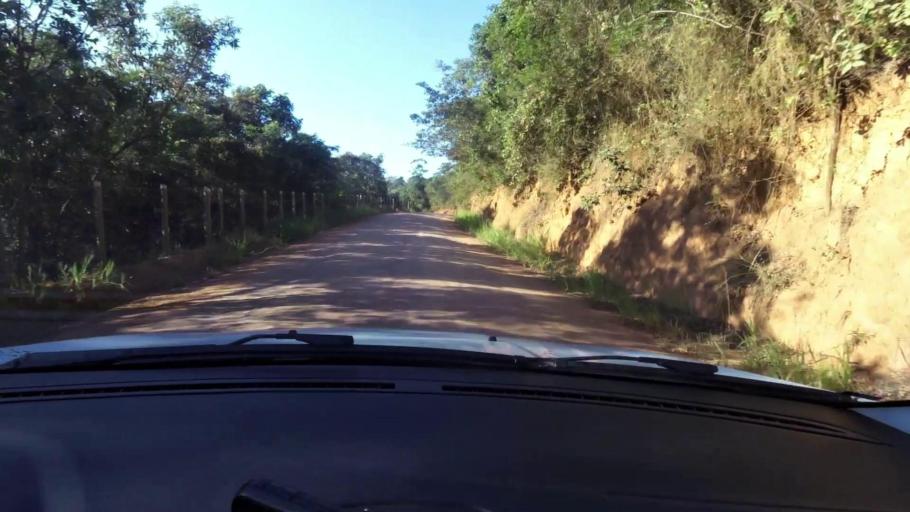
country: BR
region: Espirito Santo
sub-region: Guarapari
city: Guarapari
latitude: -20.7267
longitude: -40.5889
